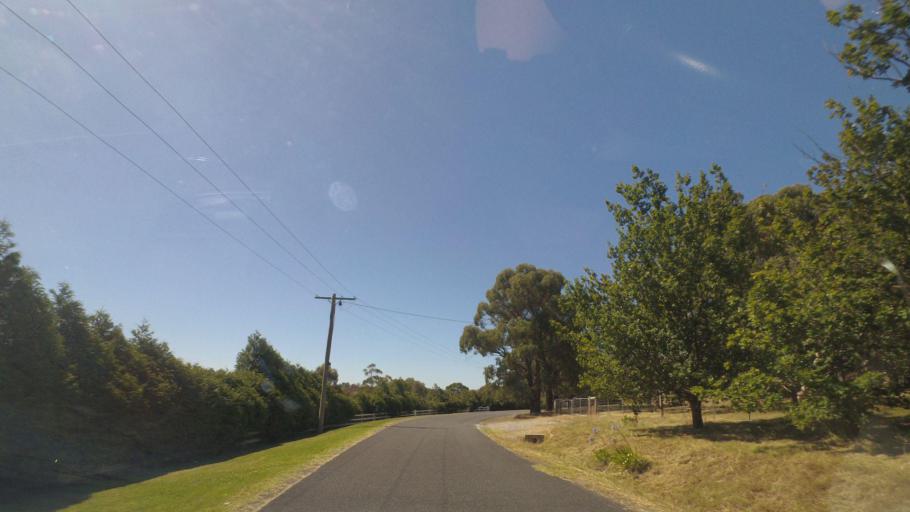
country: AU
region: Victoria
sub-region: Yarra Ranges
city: Chirnside Park
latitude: -37.7404
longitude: 145.3330
